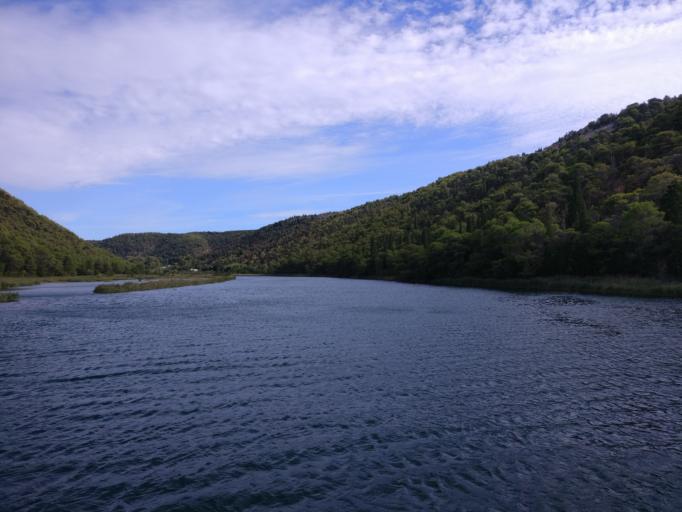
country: HR
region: Sibensko-Kniniska
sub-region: Grad Sibenik
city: Sibenik
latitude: 43.8158
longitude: 15.9508
